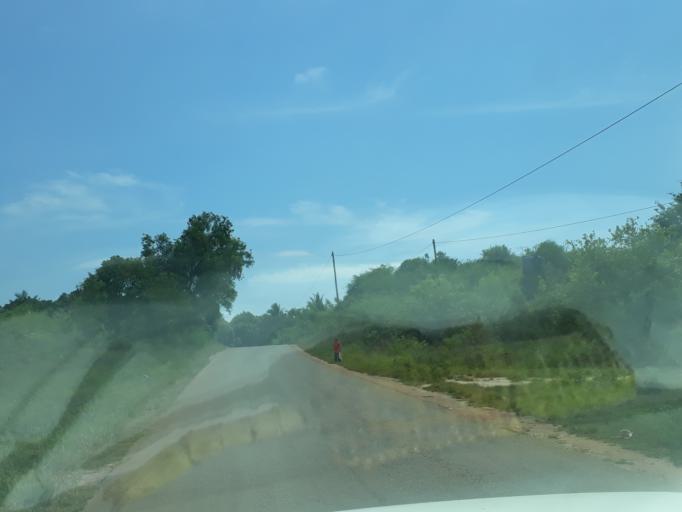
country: TZ
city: Kiwengwa
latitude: -5.9935
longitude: 39.3482
